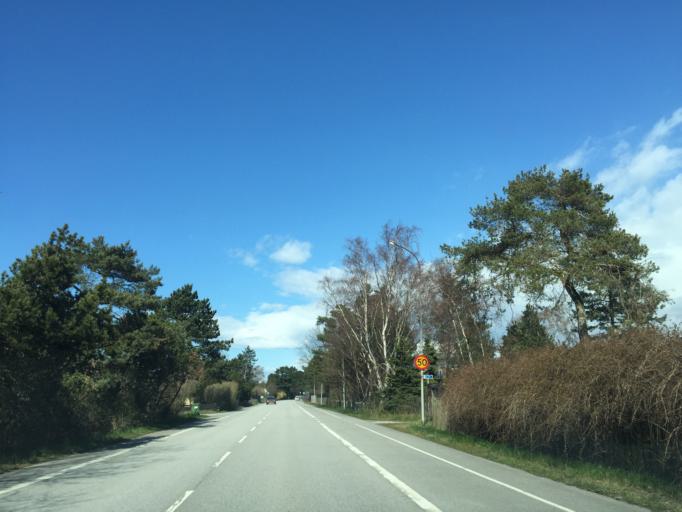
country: SE
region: Skane
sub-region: Vellinge Kommun
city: Skanor med Falsterbo
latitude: 55.3992
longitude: 12.8363
